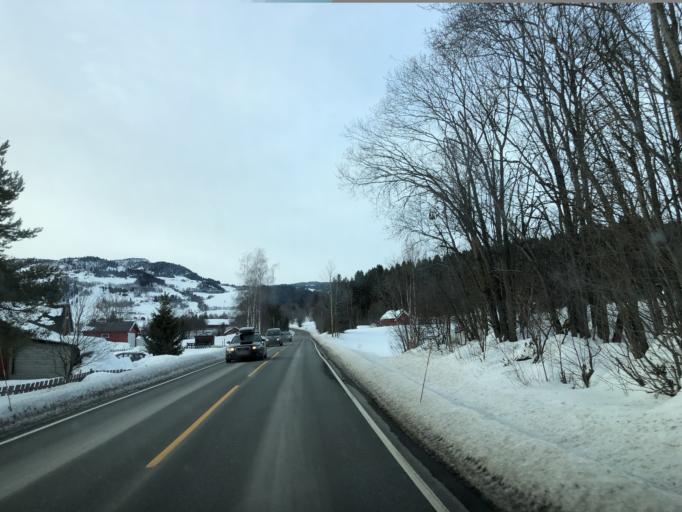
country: NO
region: Oppland
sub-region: Gausdal
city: Segalstad bru
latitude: 61.2638
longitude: 10.1555
